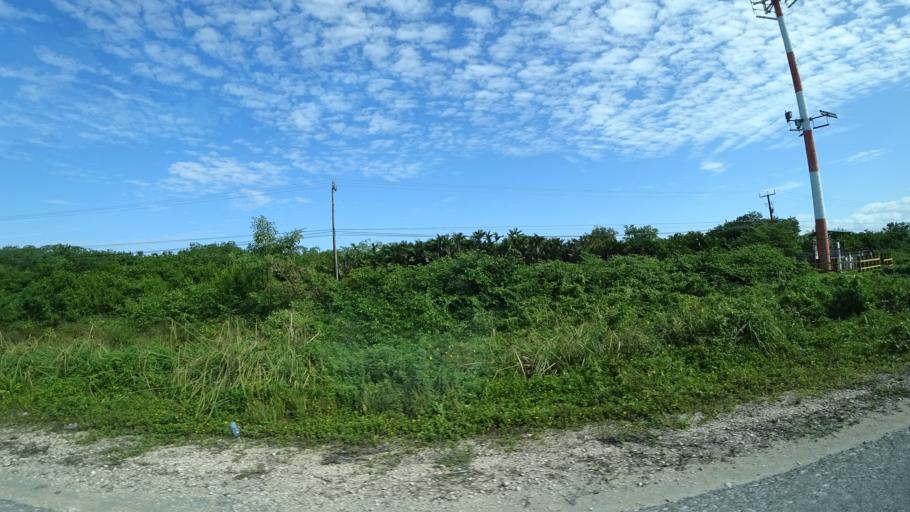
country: BZ
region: Belize
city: Belize City
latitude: 17.5418
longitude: -88.2533
